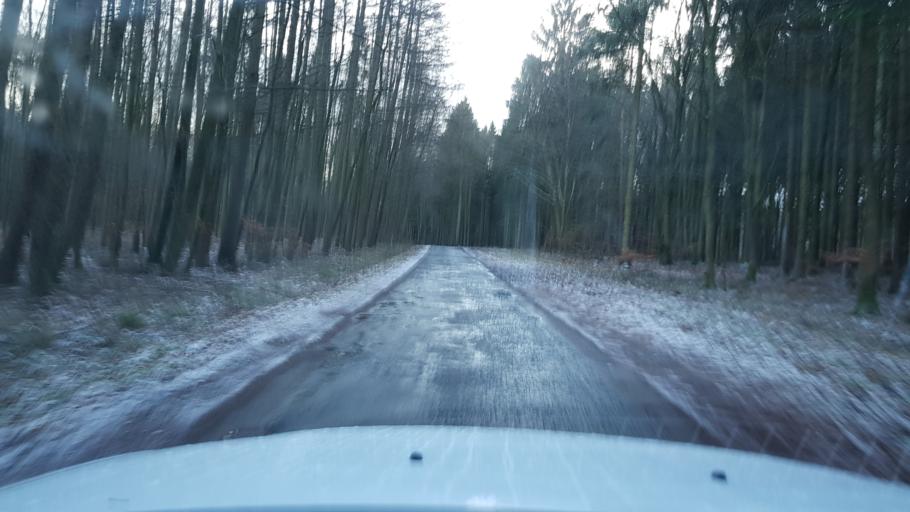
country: PL
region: West Pomeranian Voivodeship
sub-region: Powiat gryficki
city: Trzebiatow
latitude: 54.0441
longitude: 15.3294
